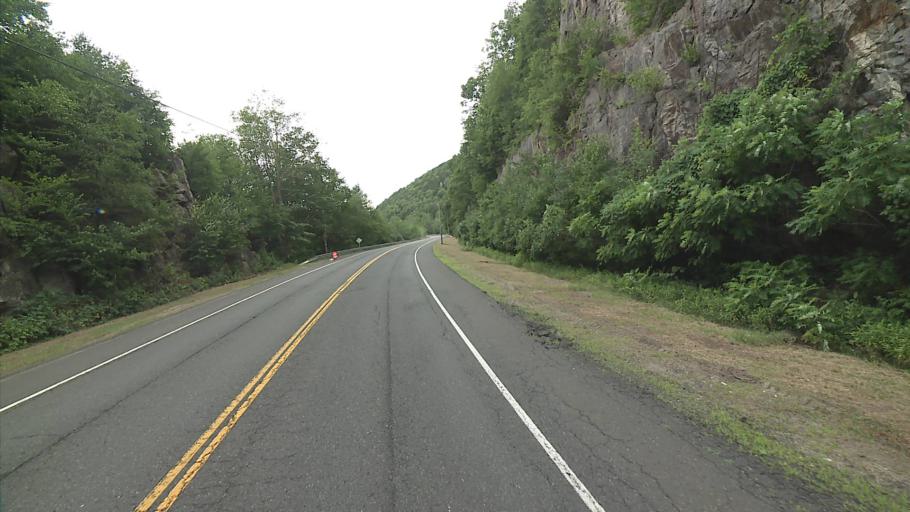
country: US
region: Connecticut
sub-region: Litchfield County
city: Winsted
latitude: 42.0119
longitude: -73.0491
